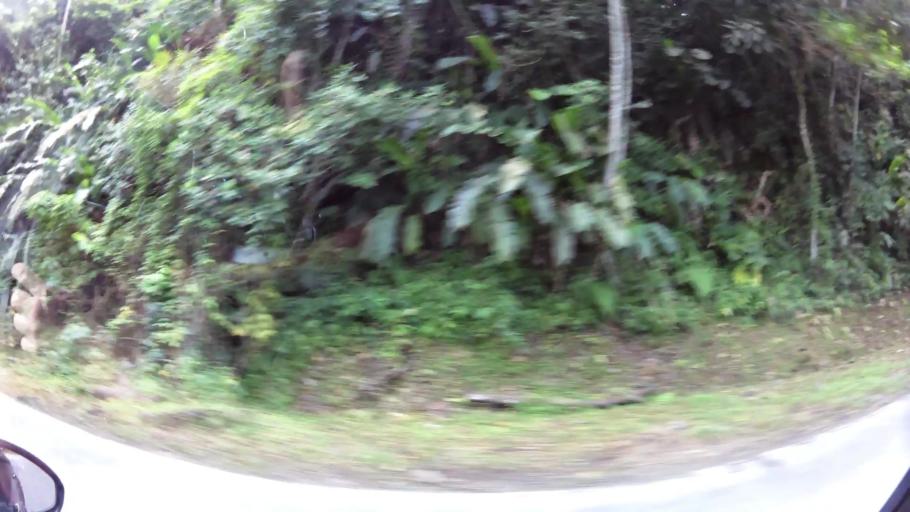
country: TT
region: Diego Martin
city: Petit Valley
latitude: 10.7472
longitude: -61.4819
